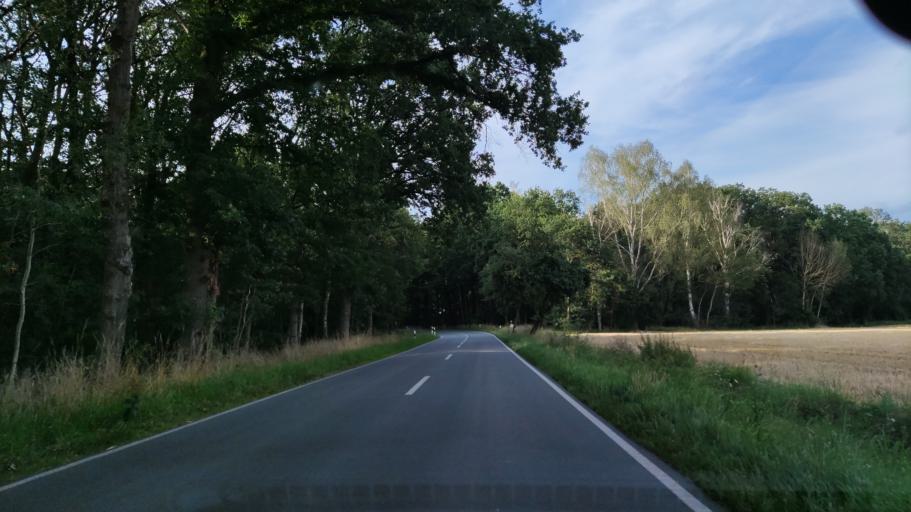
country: DE
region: Lower Saxony
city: Dannenberg
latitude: 53.1123
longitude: 11.1125
